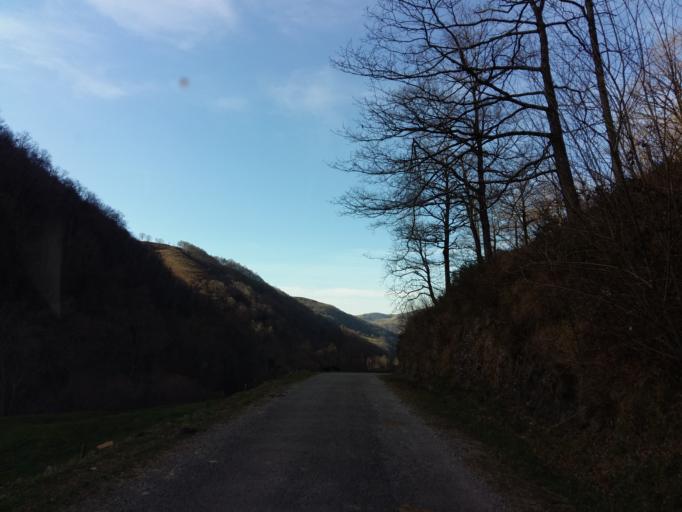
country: ES
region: Cantabria
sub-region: Provincia de Cantabria
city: Vega de Pas
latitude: 43.1346
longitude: -3.7879
